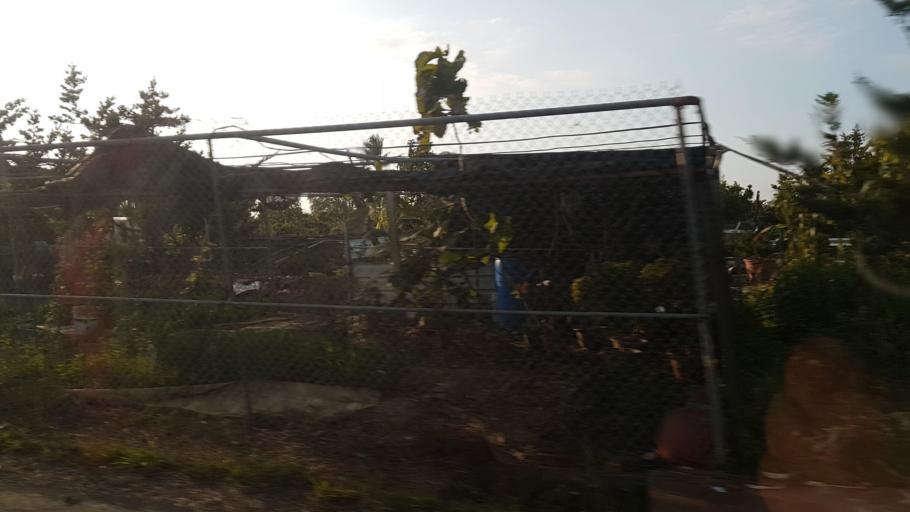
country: TW
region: Taiwan
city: Xinying
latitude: 23.3351
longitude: 120.3237
